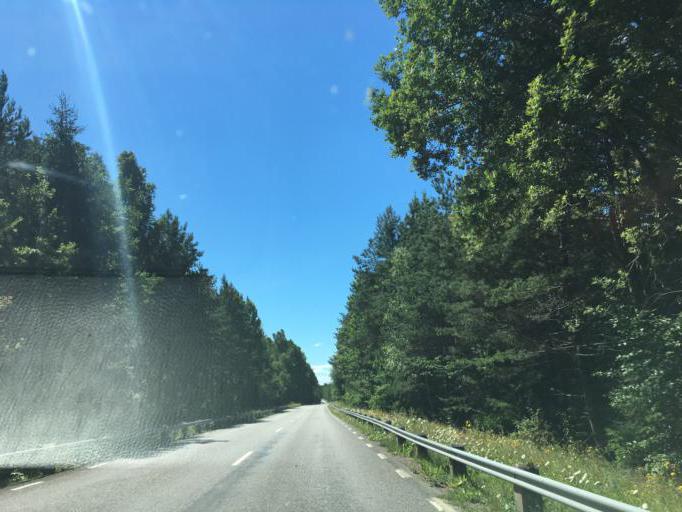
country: SE
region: OErebro
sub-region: Laxa Kommun
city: Laxa
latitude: 58.8446
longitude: 14.5484
